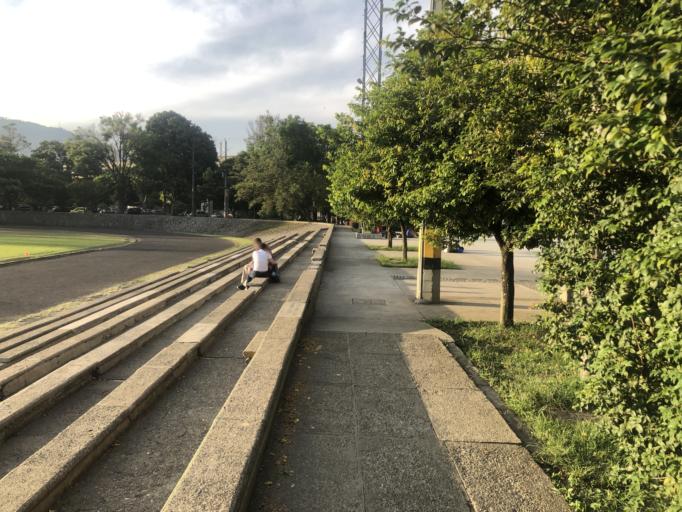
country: CO
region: Antioquia
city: Medellin
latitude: 6.2694
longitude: -75.5691
